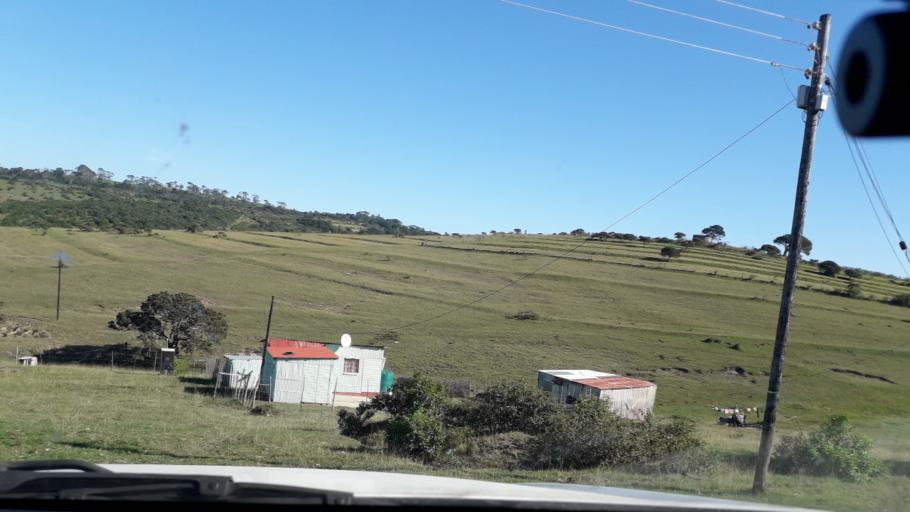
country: ZA
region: Eastern Cape
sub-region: Buffalo City Metropolitan Municipality
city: East London
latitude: -32.8438
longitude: 27.9854
